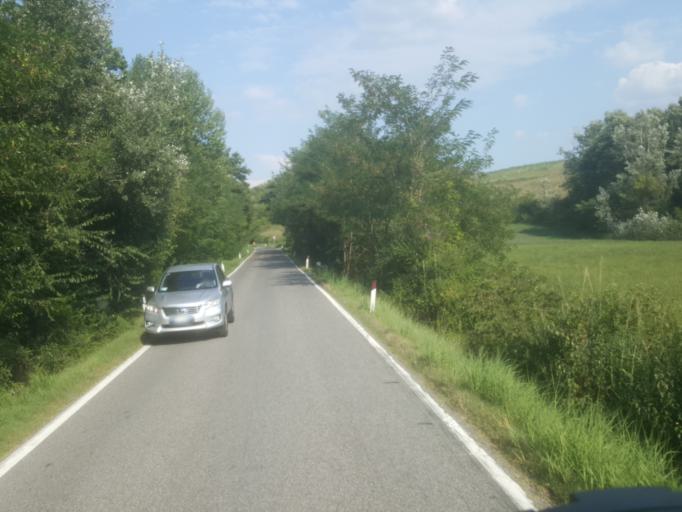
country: IT
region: Tuscany
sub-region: Province of Pisa
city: Volterra
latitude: 43.4507
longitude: 10.8080
